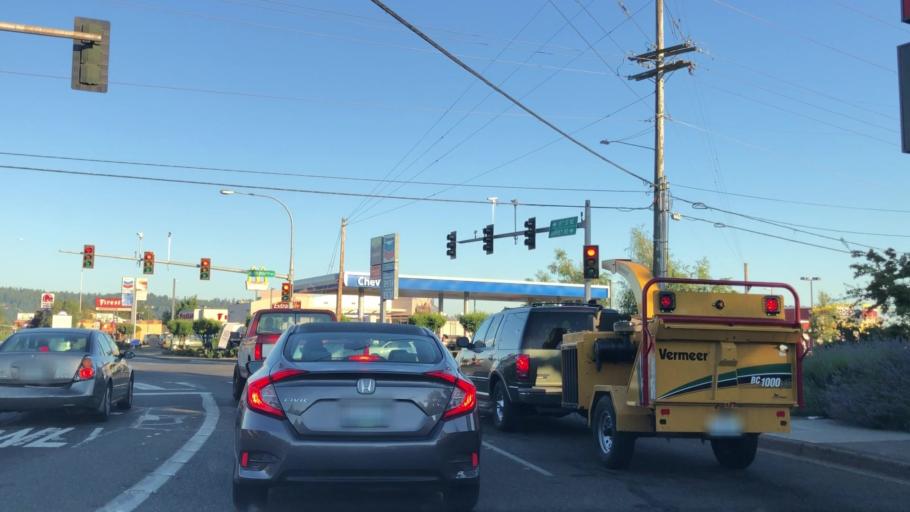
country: US
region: Washington
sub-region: King County
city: Auburn
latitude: 47.3209
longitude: -122.2210
